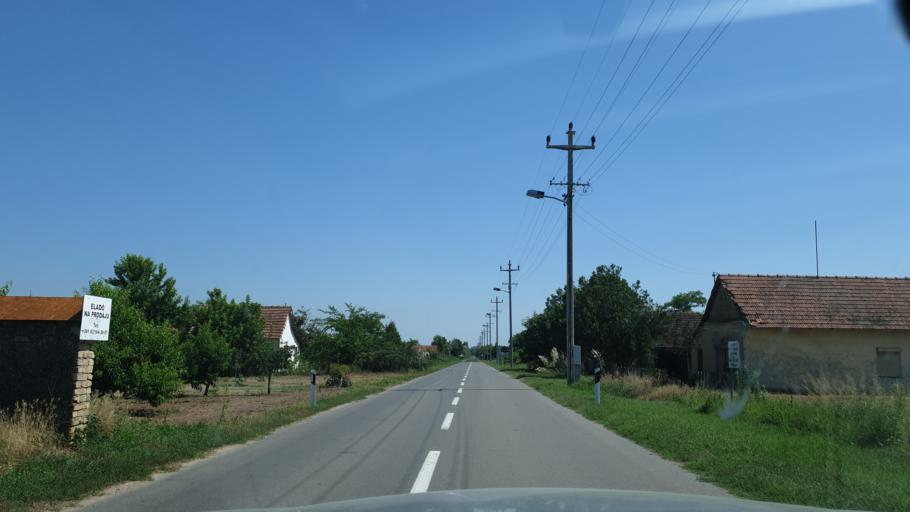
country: HU
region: Csongrad
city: Morahalom
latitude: 46.1403
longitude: 19.8475
